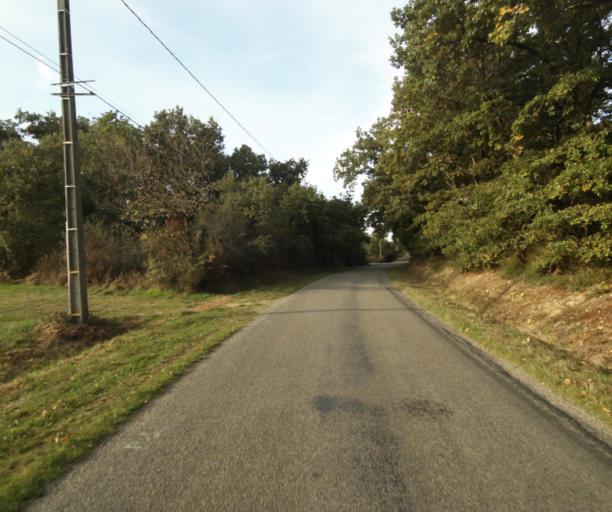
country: FR
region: Midi-Pyrenees
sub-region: Departement du Tarn-et-Garonne
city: Campsas
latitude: 43.8780
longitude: 1.3239
